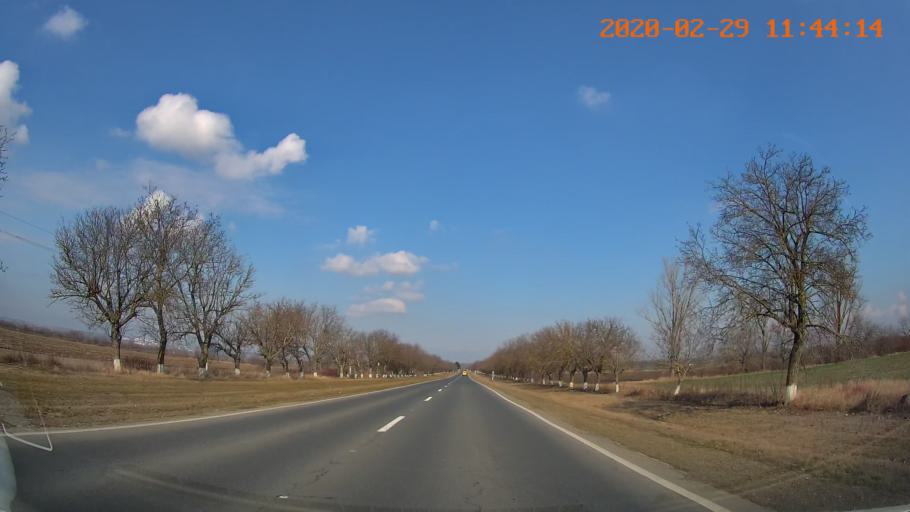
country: MD
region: Rezina
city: Saharna
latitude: 47.7081
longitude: 29.0010
